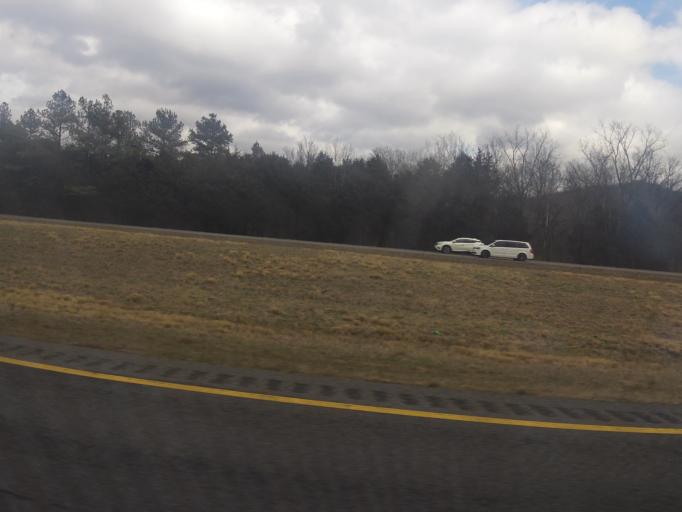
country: US
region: Tennessee
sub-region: Rutherford County
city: Plainview
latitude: 35.6674
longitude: -86.2780
